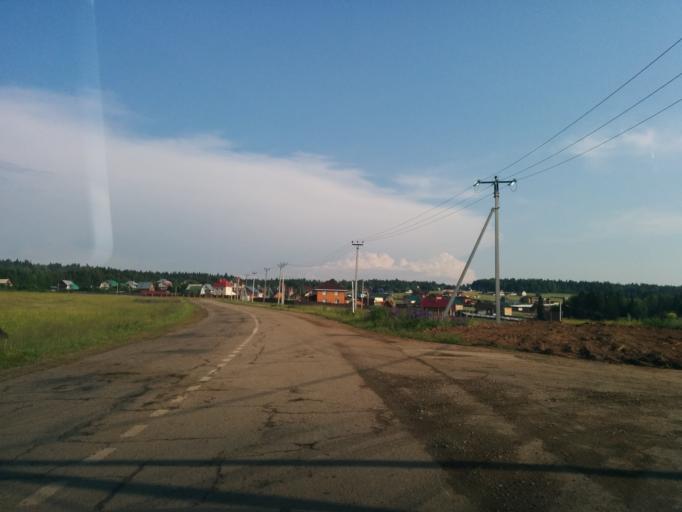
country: RU
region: Perm
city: Polazna
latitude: 58.2541
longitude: 56.2641
